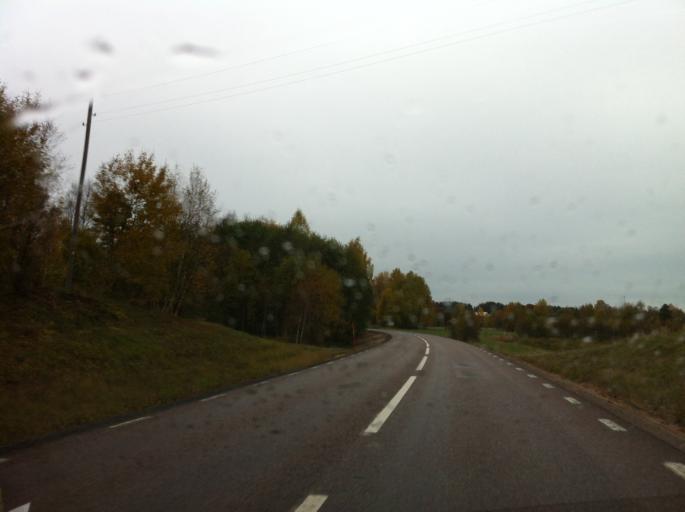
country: SE
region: Dalarna
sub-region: Ludvika Kommun
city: Grangesberg
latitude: 60.2650
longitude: 14.9836
